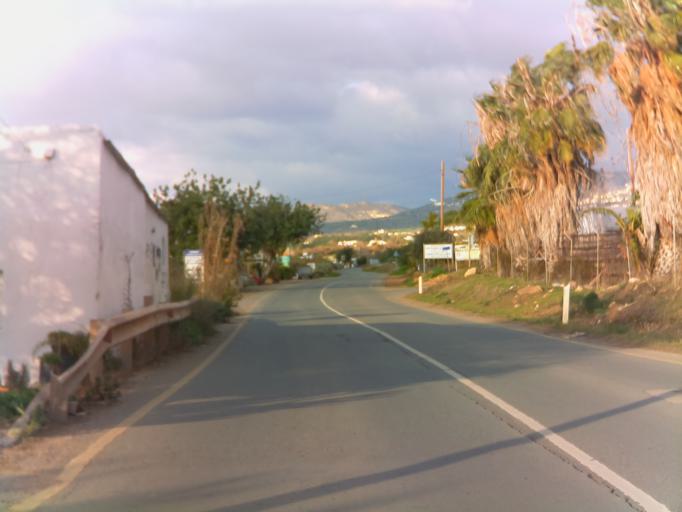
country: CY
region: Pafos
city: Kissonerga
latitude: 34.8121
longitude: 32.4103
